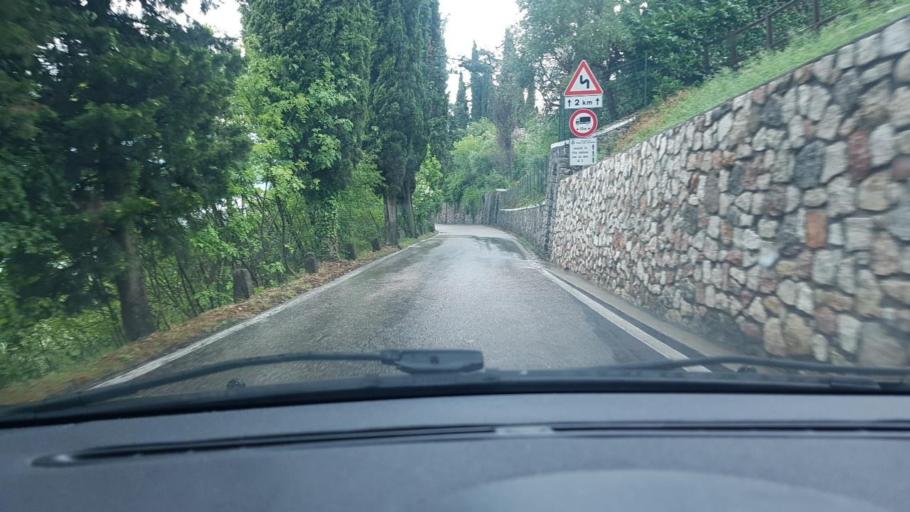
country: IT
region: Veneto
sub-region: Provincia di Verona
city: Torri del Benaco
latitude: 45.6070
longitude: 10.7002
